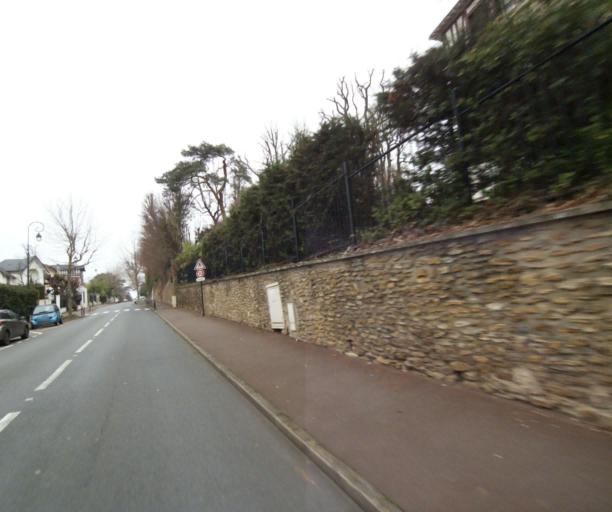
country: FR
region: Ile-de-France
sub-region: Departement des Hauts-de-Seine
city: Garches
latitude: 48.8425
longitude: 2.1776
